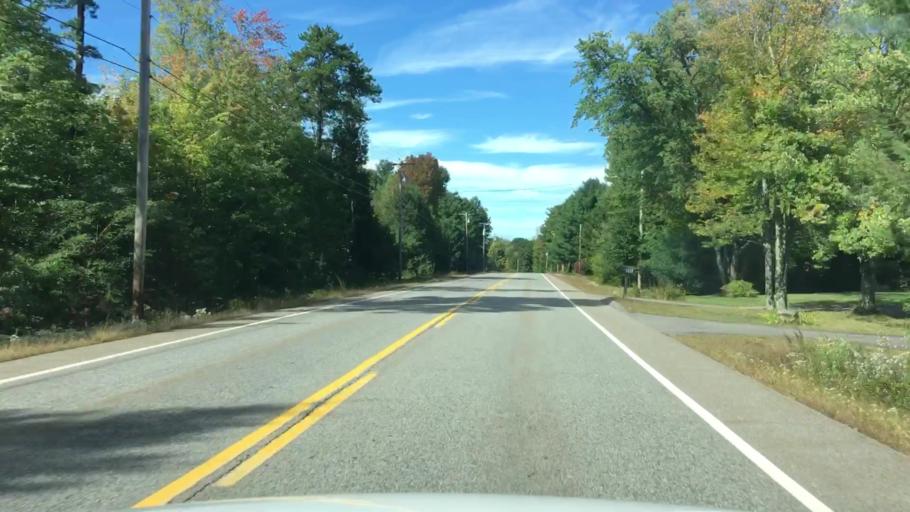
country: US
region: Maine
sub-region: Cumberland County
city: Westbrook
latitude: 43.6532
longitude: -70.3989
